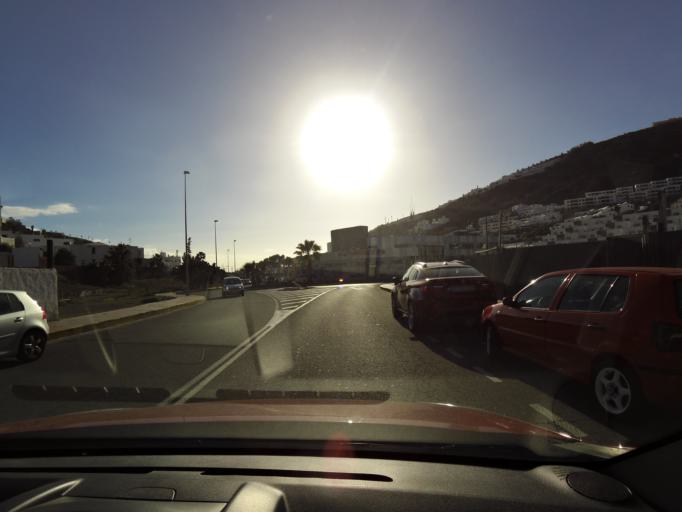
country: ES
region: Canary Islands
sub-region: Provincia de Las Palmas
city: Puerto Rico
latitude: 27.7938
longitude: -15.7064
